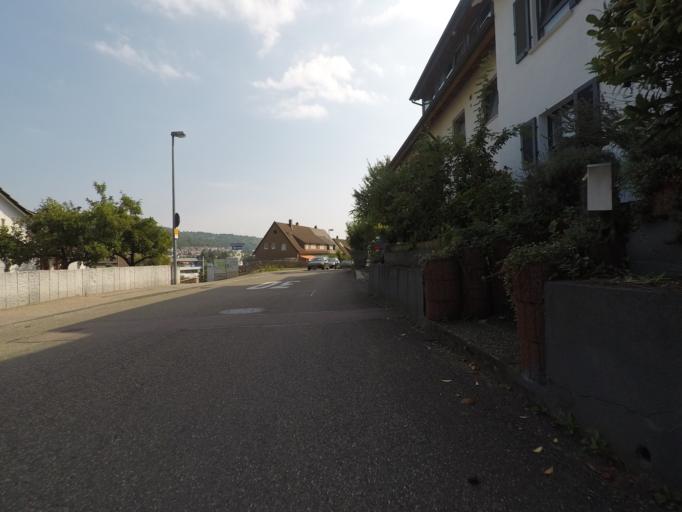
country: DE
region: Baden-Wuerttemberg
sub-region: Regierungsbezirk Stuttgart
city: Winterbach
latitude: 48.8050
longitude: 9.4360
